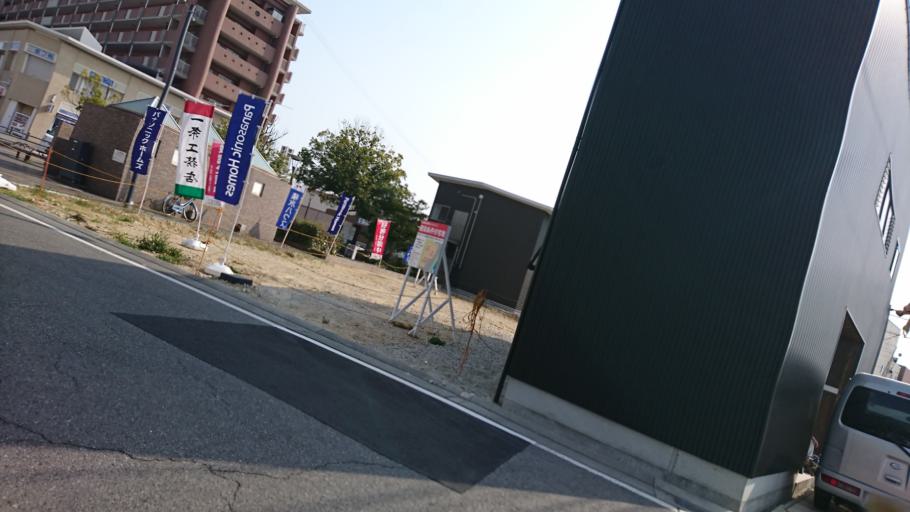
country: JP
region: Hyogo
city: Kakogawacho-honmachi
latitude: 34.7172
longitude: 134.8683
